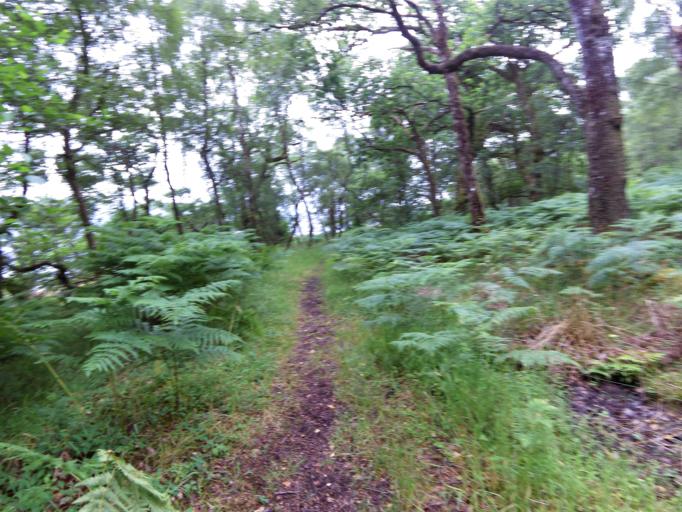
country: GB
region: Scotland
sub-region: Highland
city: Fort William
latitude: 56.8326
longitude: -5.1236
